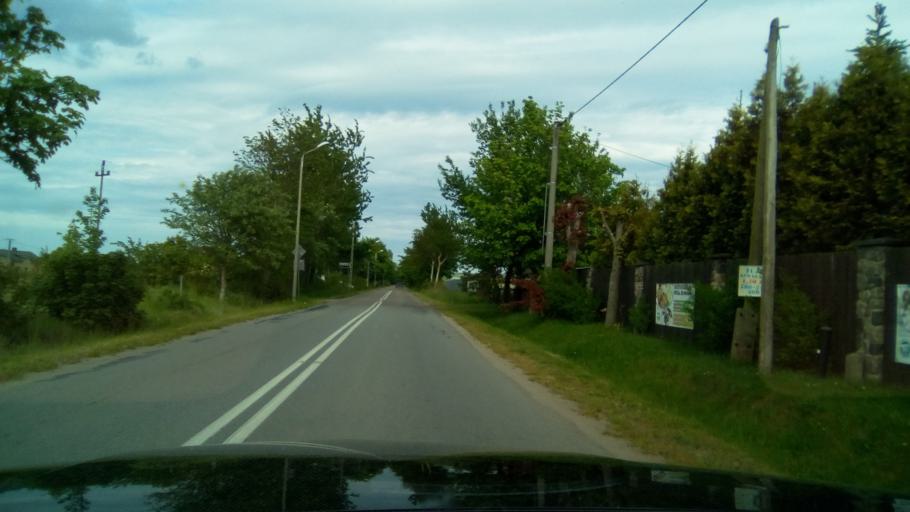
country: PL
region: Pomeranian Voivodeship
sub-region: Powiat pucki
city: Krokowa
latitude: 54.8078
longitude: 18.1784
